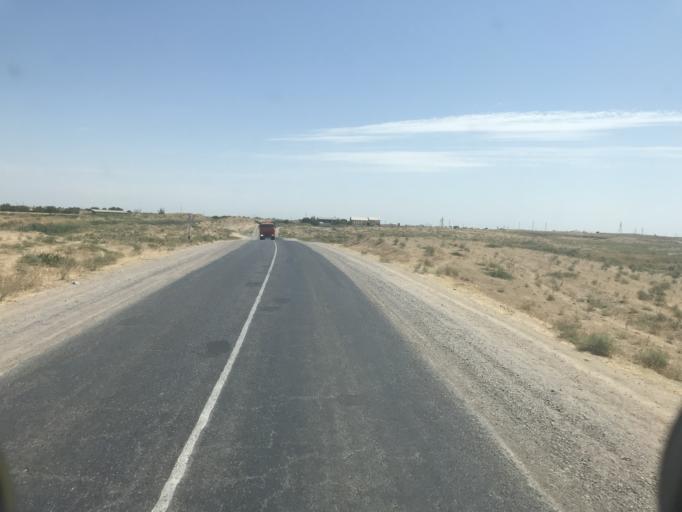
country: UZ
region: Toshkent
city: Yangiyul
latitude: 41.3378
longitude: 68.8804
